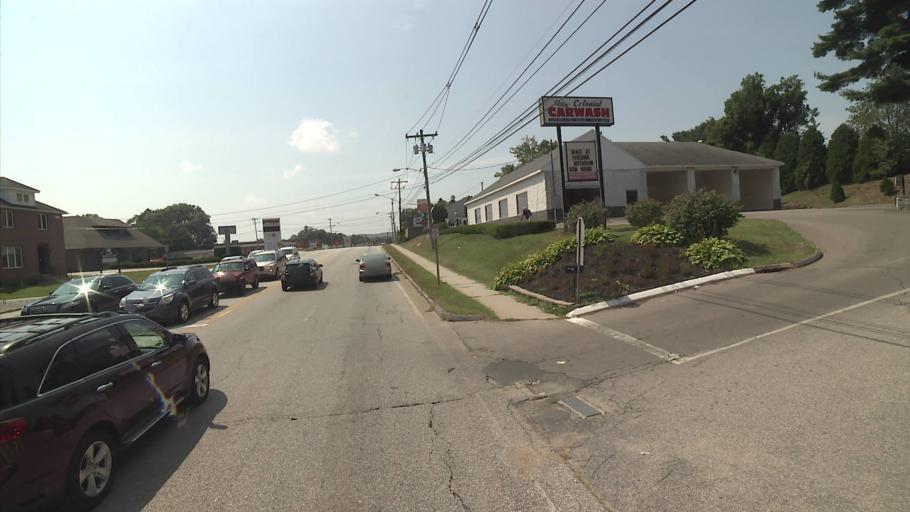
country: US
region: Connecticut
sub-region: New London County
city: Norwich
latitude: 41.5168
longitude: -72.0992
